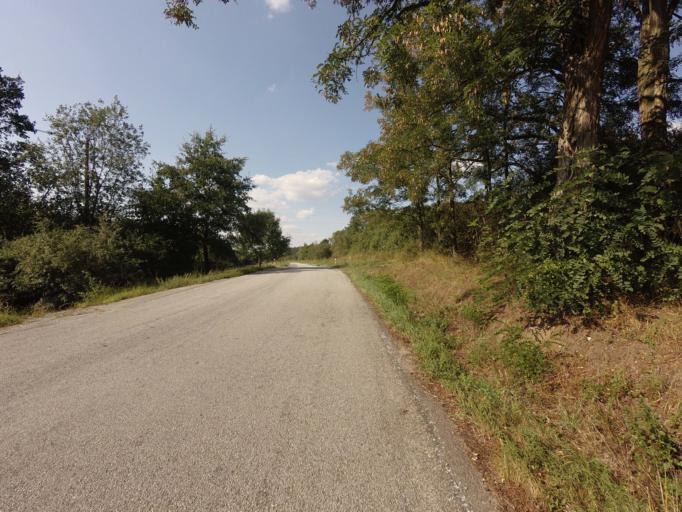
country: CZ
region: Jihocesky
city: Tyn nad Vltavou
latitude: 49.2016
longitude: 14.4457
